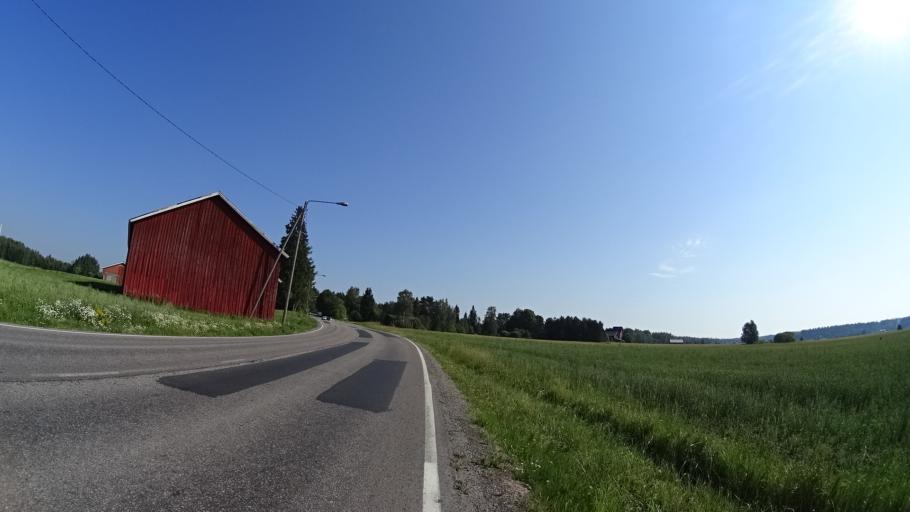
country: FI
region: Uusimaa
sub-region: Helsinki
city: Vantaa
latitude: 60.3110
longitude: 25.0700
